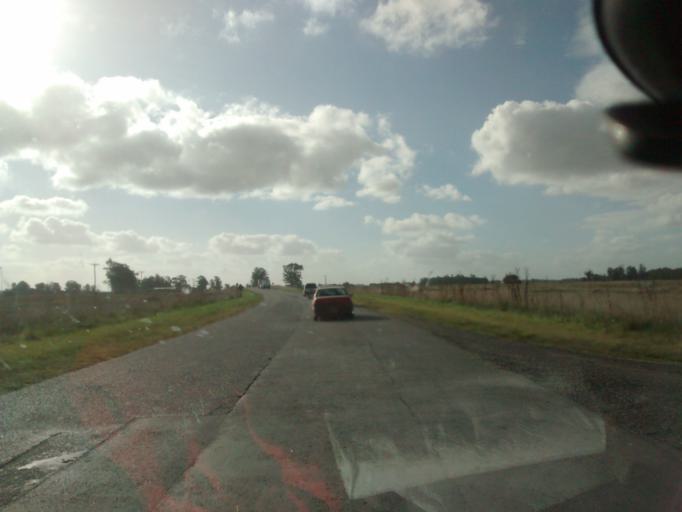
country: AR
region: Buenos Aires
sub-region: Partido de Ayacucho
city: Ayacucho
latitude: -37.1799
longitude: -58.5150
